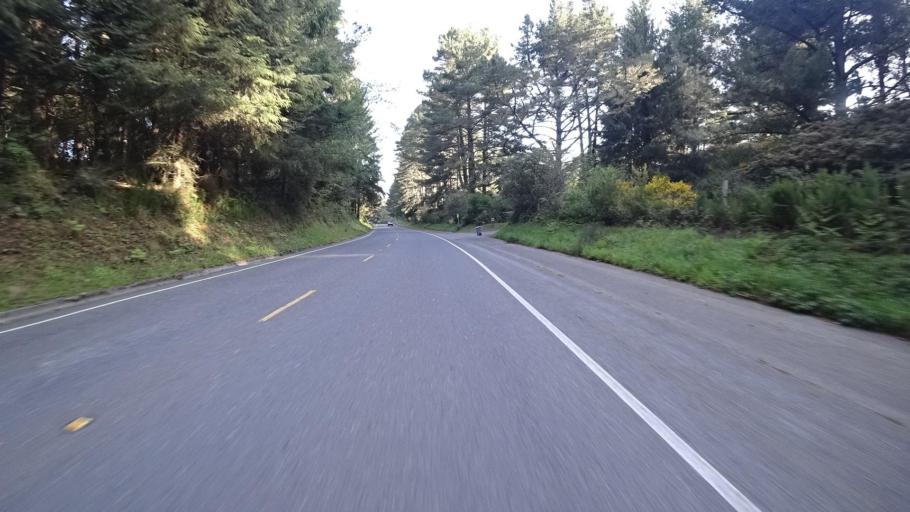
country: US
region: California
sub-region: Humboldt County
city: Humboldt Hill
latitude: 40.7243
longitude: -124.2012
